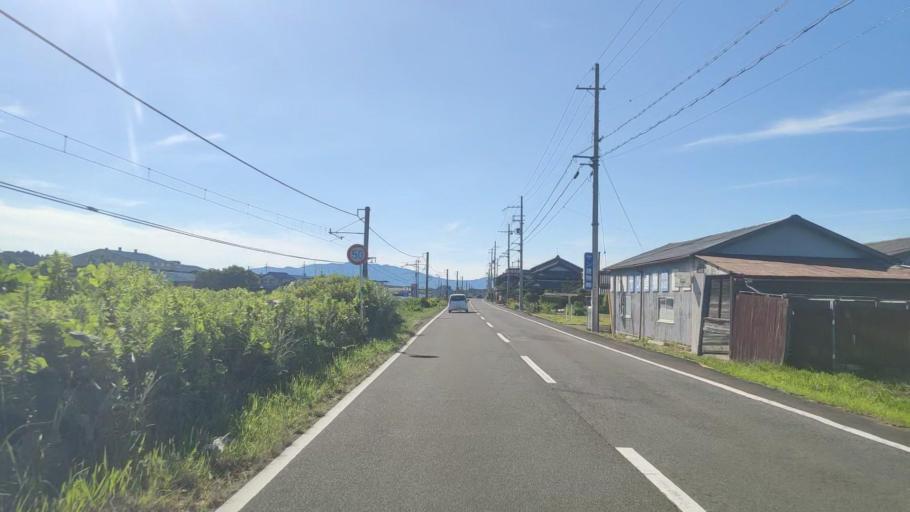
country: JP
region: Shiga Prefecture
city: Minakuchicho-matoba
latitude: 34.8954
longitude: 136.2219
